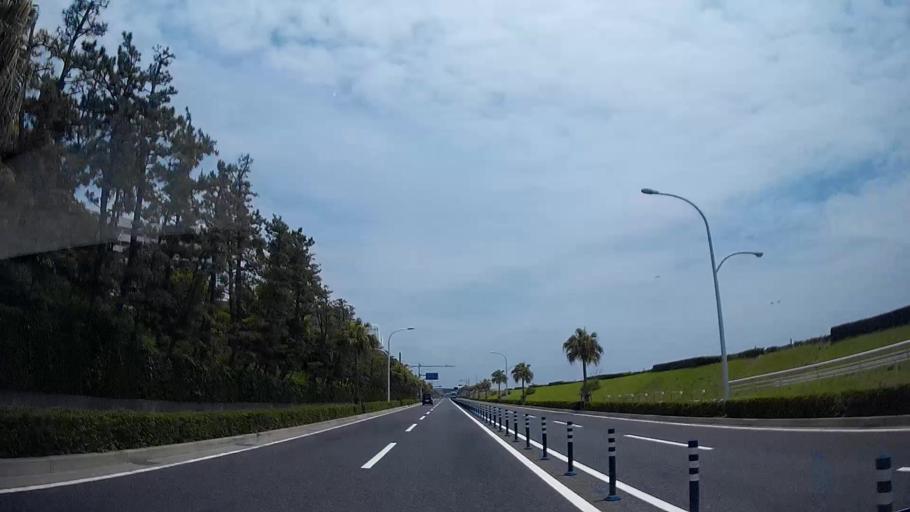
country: JP
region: Tokyo
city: Urayasu
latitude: 35.6251
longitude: 139.8769
